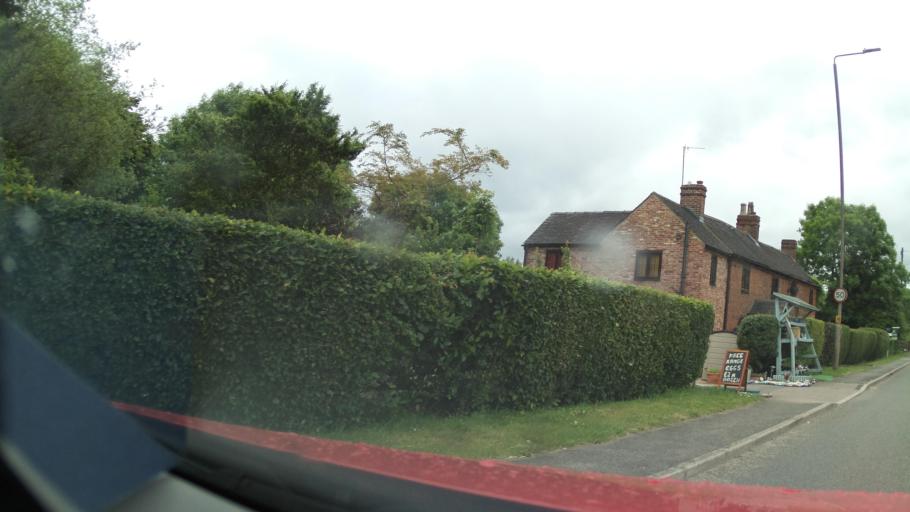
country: GB
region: England
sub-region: Derbyshire
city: Rodsley
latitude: 52.8769
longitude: -1.6964
